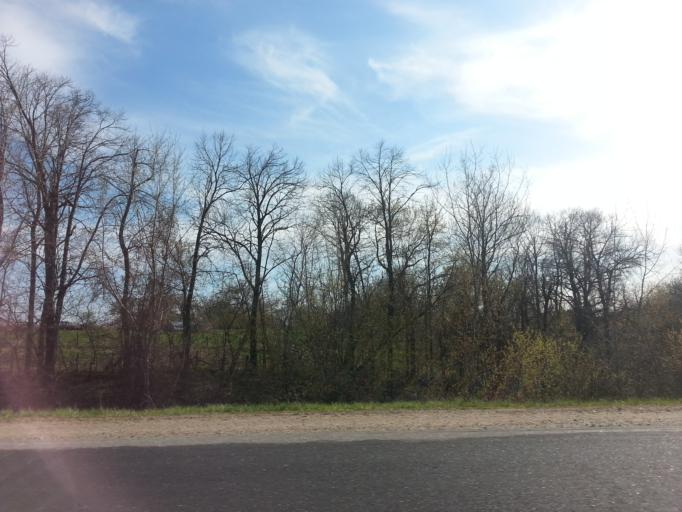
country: US
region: Wisconsin
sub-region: Pierce County
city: Ellsworth
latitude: 44.6813
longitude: -92.6079
